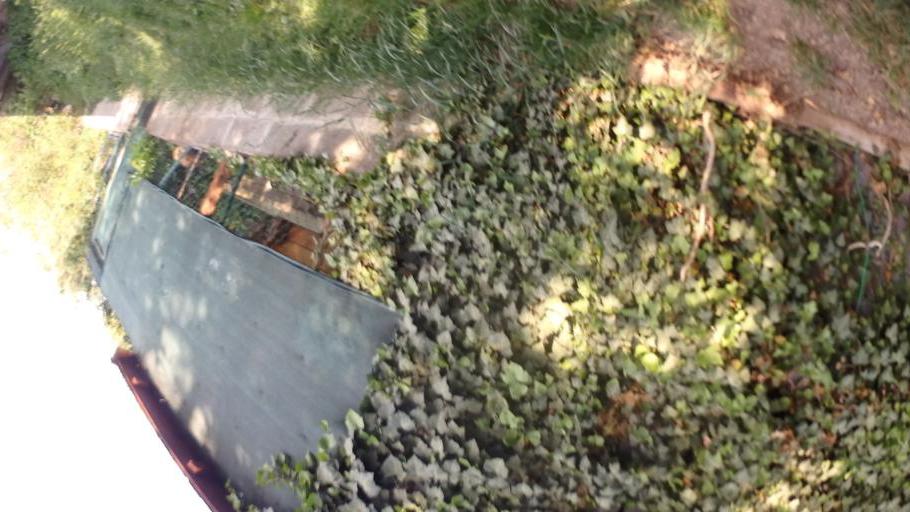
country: CZ
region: South Moravian
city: Moravany
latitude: 49.1489
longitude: 16.5810
